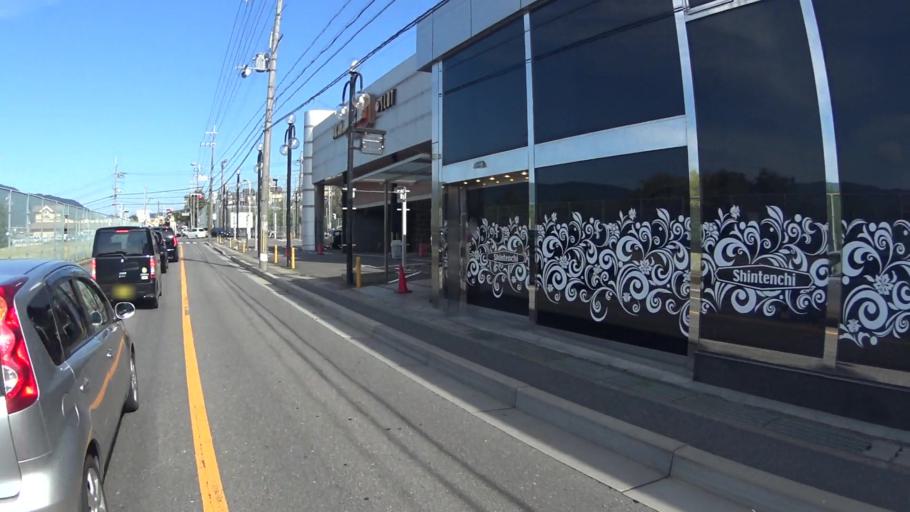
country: JP
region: Kyoto
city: Muko
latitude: 34.9473
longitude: 135.6952
